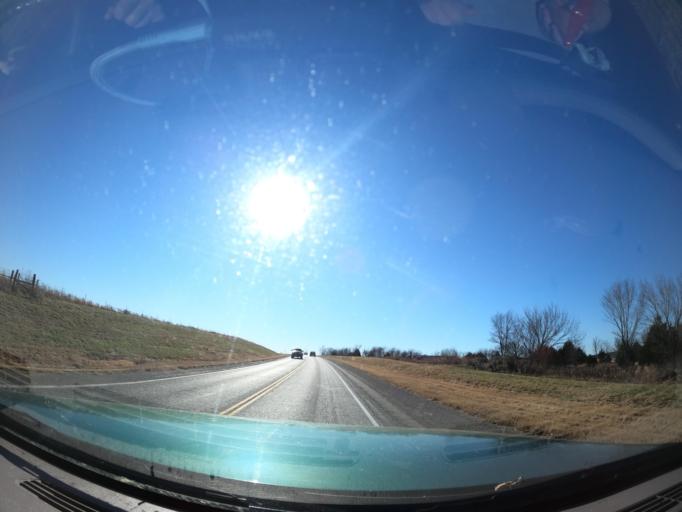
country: US
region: Oklahoma
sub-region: Muskogee County
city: Haskell
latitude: 35.8655
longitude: -95.6756
